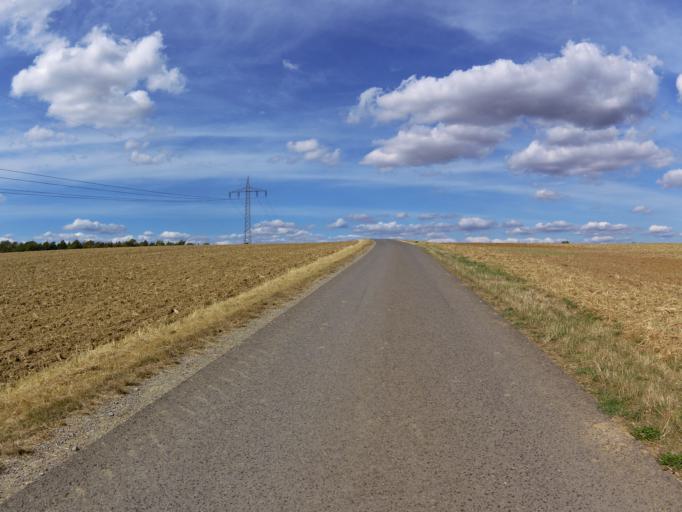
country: DE
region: Bavaria
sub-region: Regierungsbezirk Unterfranken
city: Guntersleben
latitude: 49.8668
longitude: 9.9153
